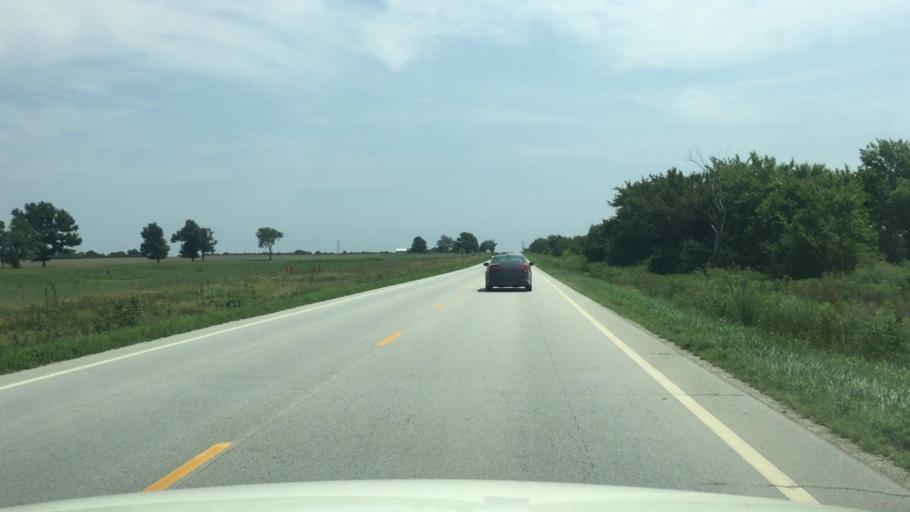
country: US
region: Kansas
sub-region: Cherokee County
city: Columbus
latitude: 37.1792
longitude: -94.9218
